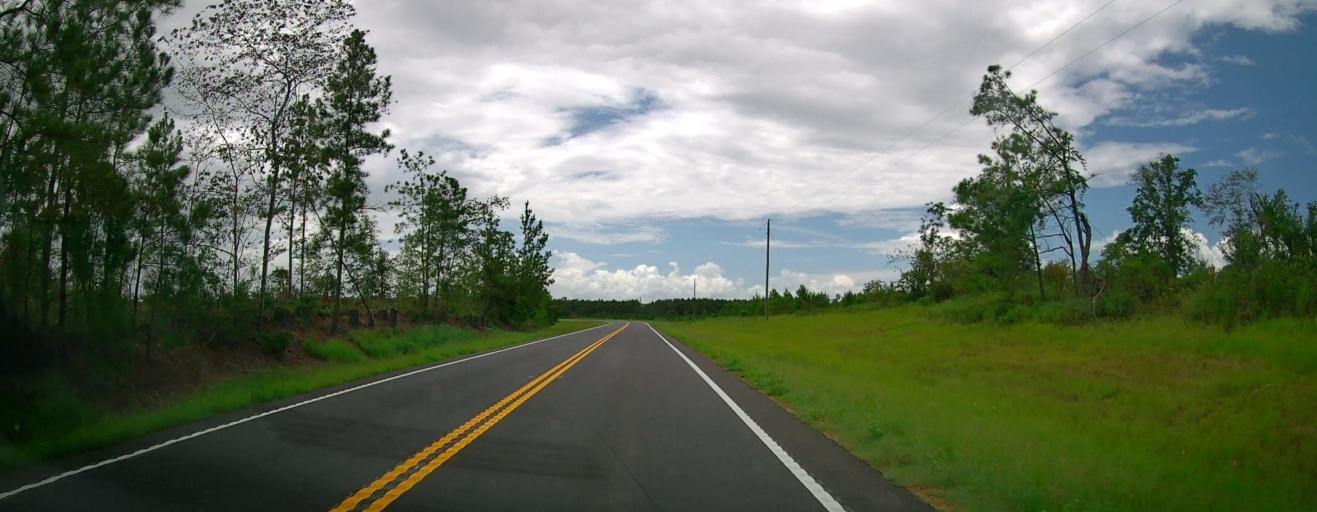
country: US
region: Georgia
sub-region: Pulaski County
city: Hawkinsville
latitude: 32.1665
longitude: -83.5442
